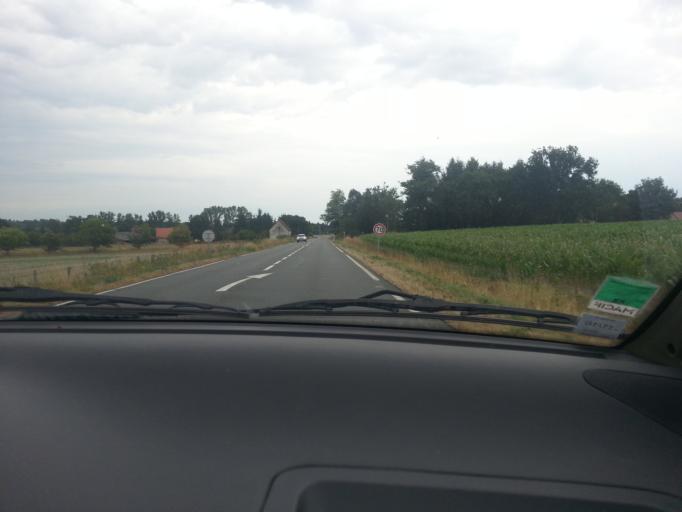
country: FR
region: Auvergne
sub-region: Departement de l'Allier
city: Saint-Gerand-le-Puy
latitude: 46.2030
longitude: 3.4986
